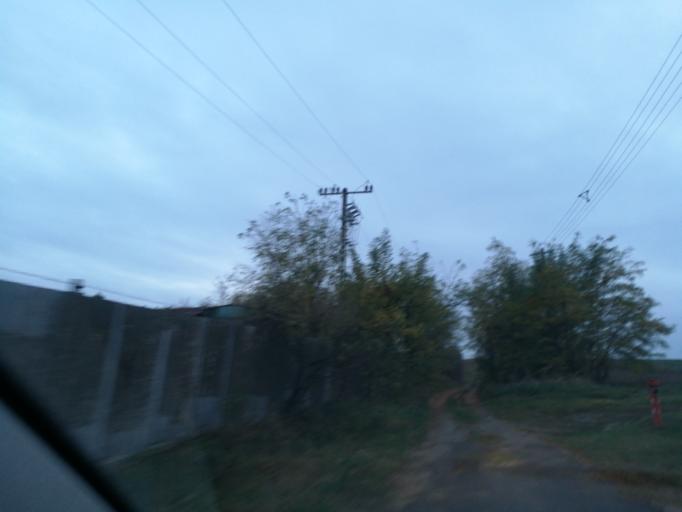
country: HU
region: Nograd
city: Bujak
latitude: 47.8746
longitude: 19.5565
